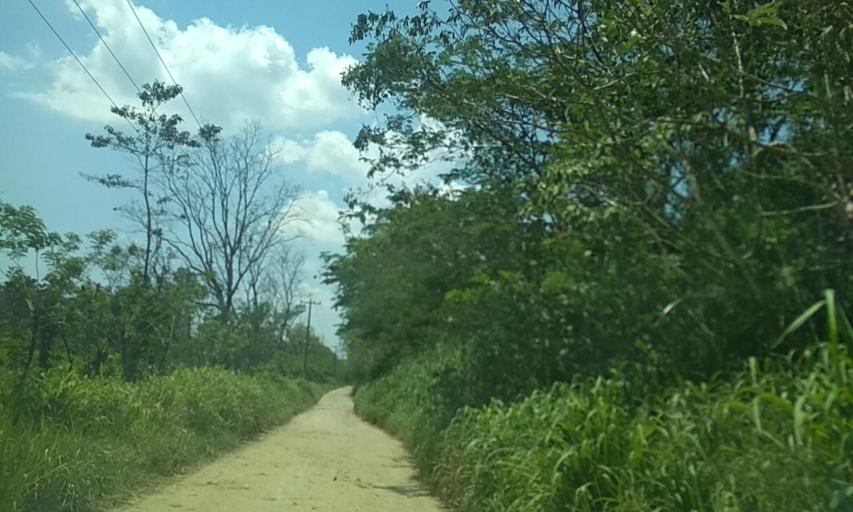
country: MX
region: Chiapas
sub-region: Tecpatan
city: Raudales Malpaso
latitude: 17.2846
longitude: -93.8365
